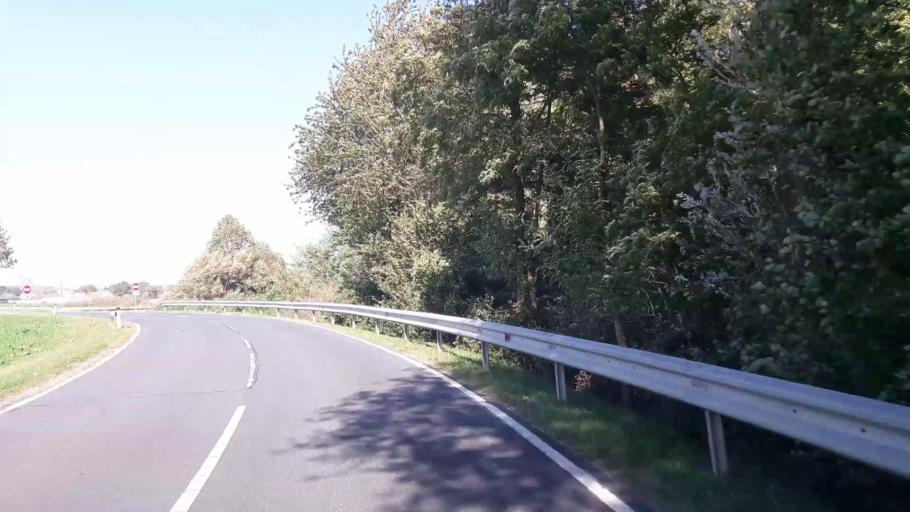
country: AT
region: Lower Austria
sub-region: Politischer Bezirk Korneuburg
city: Ernstbrunn
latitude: 48.4901
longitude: 16.3703
